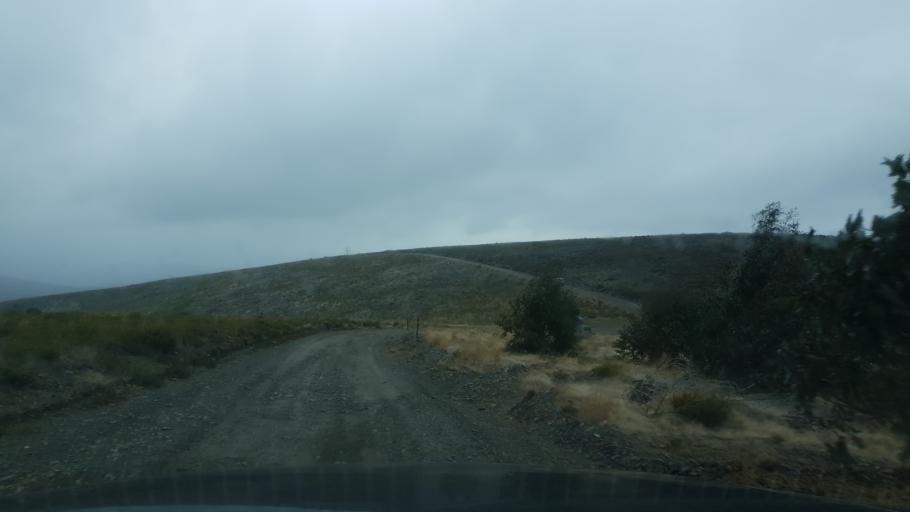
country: PT
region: Viseu
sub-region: Sao Pedro do Sul
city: Sao Pedro do Sul
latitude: 40.8535
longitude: -8.1047
